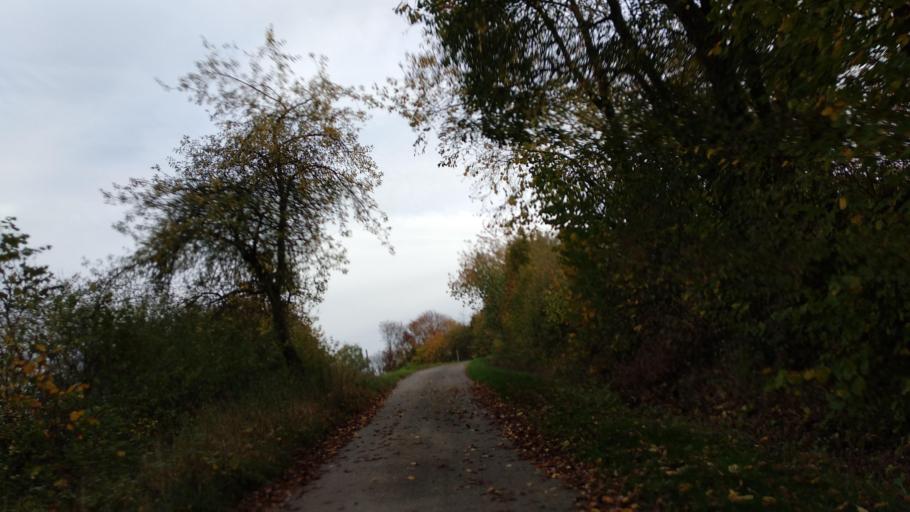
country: DE
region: North Rhine-Westphalia
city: Beverungen
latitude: 51.6774
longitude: 9.3185
